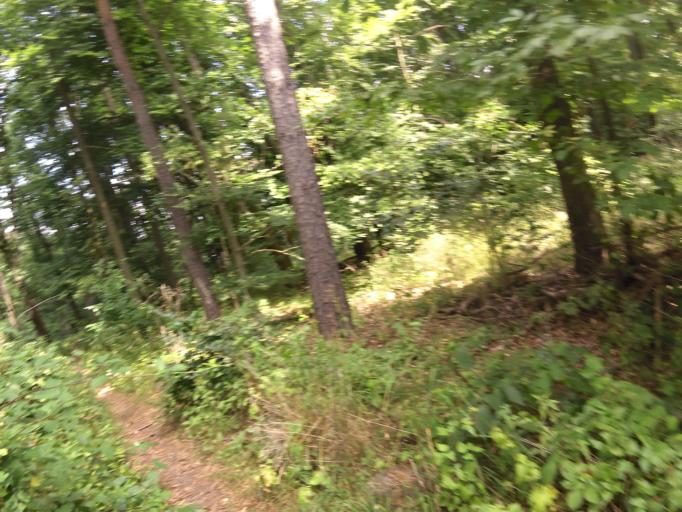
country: DE
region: Bavaria
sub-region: Regierungsbezirk Unterfranken
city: Gadheim
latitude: 49.8168
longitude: 9.9064
